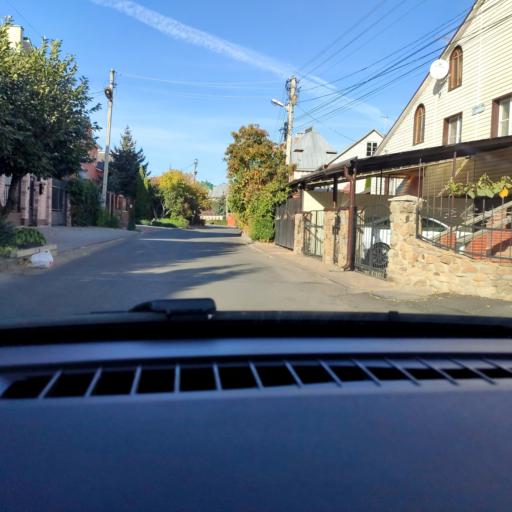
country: RU
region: Voronezj
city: Voronezh
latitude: 51.7076
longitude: 39.2012
